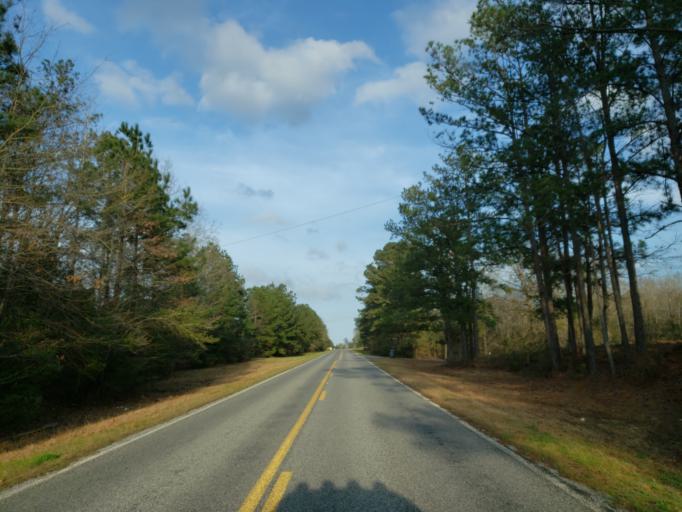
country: US
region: Mississippi
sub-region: Clarke County
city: Stonewall
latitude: 32.1723
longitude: -88.6903
